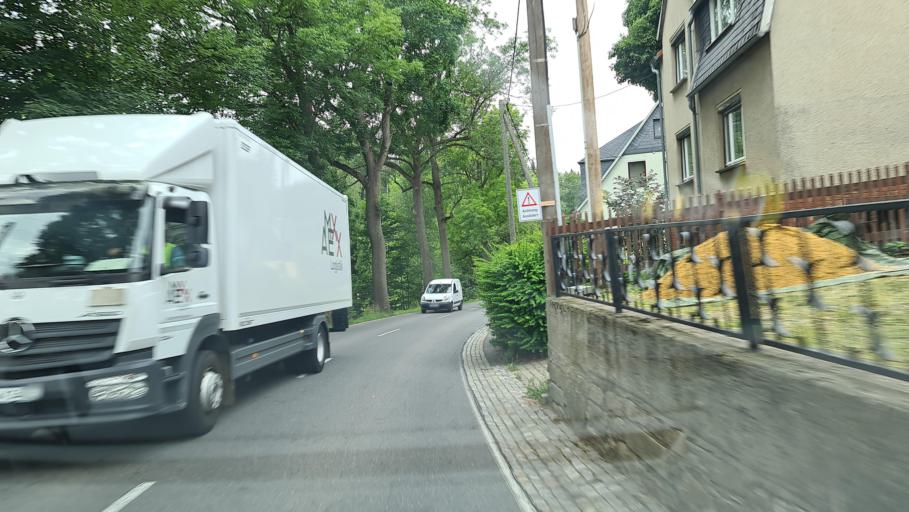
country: DE
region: Saxony
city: Stutzengrun
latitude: 50.5301
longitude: 12.5120
